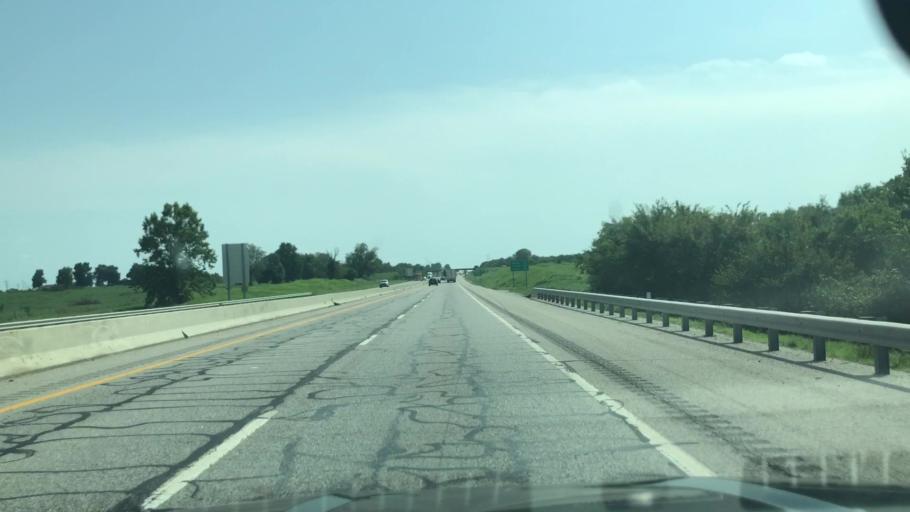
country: US
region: Oklahoma
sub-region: Ottawa County
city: Miami
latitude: 36.8521
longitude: -94.8562
